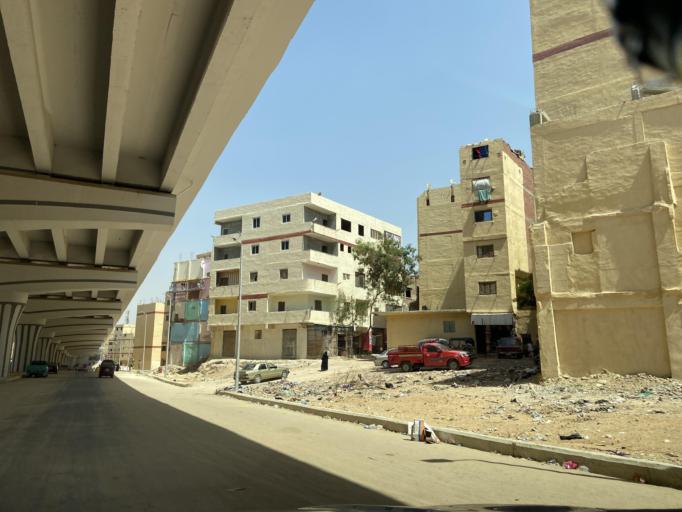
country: EG
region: Muhafazat al Qahirah
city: Cairo
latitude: 30.0659
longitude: 31.3822
